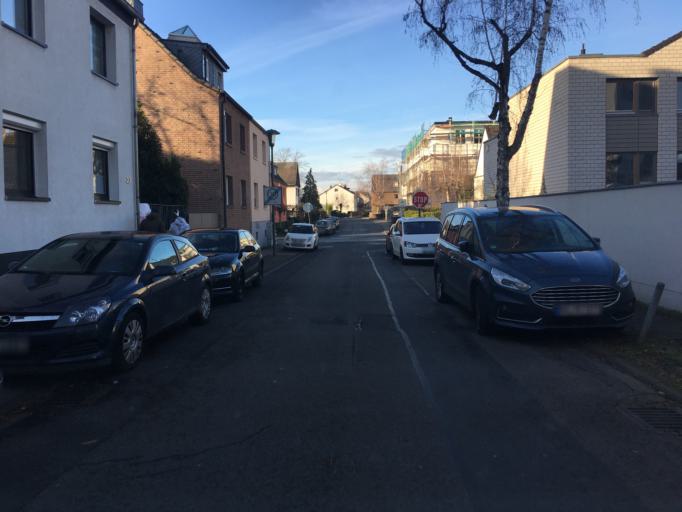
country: DE
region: North Rhine-Westphalia
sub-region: Regierungsbezirk Koln
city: Porz am Rhein
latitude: 50.8715
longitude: 7.0232
